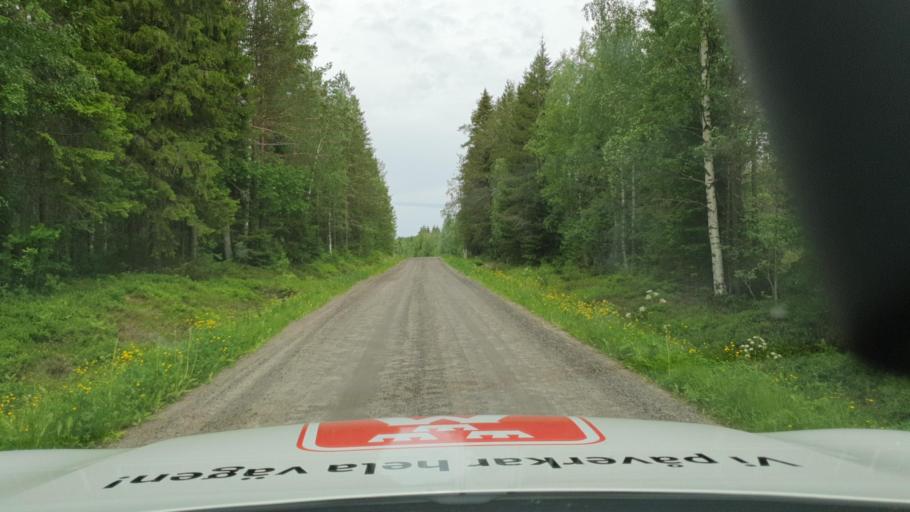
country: SE
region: Vaesterbotten
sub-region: Robertsfors Kommun
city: Robertsfors
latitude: 64.1939
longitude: 20.7145
